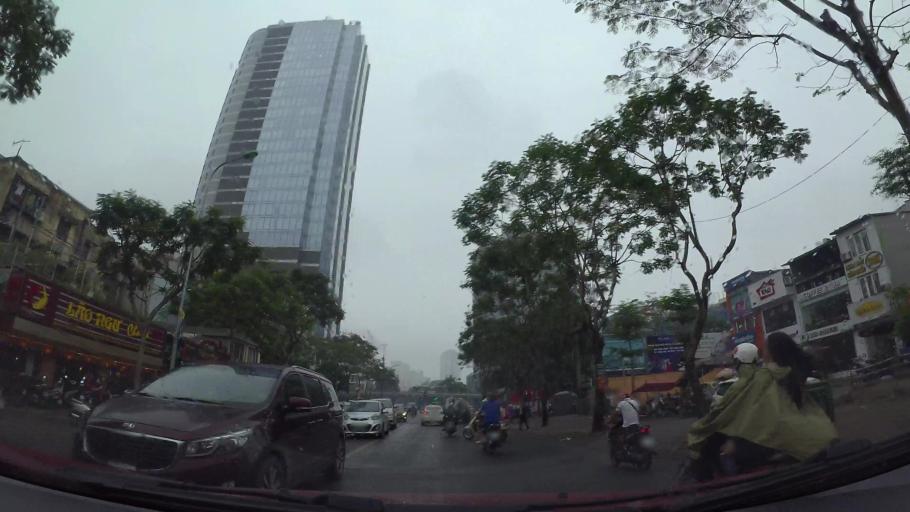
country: VN
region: Ha Noi
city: Dong Da
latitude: 21.0158
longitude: 105.8161
